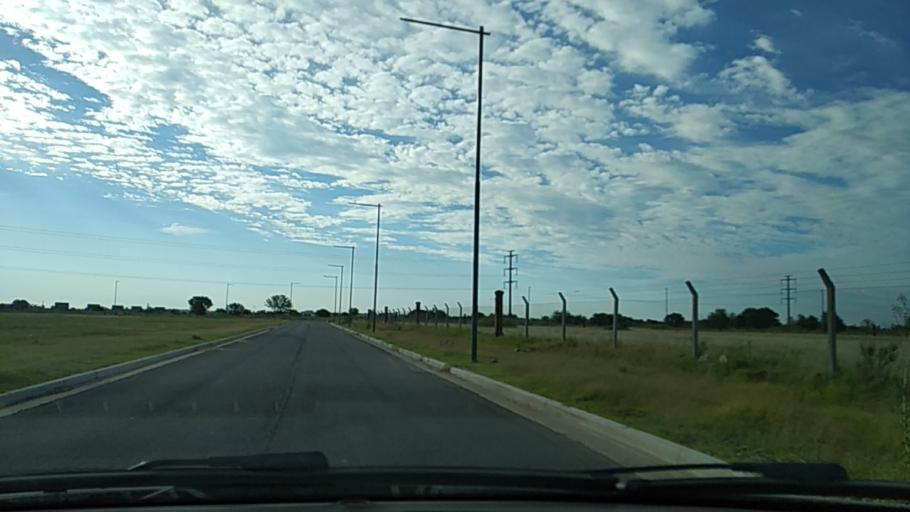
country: AR
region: Santa Fe
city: Funes
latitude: -32.9467
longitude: -60.7768
